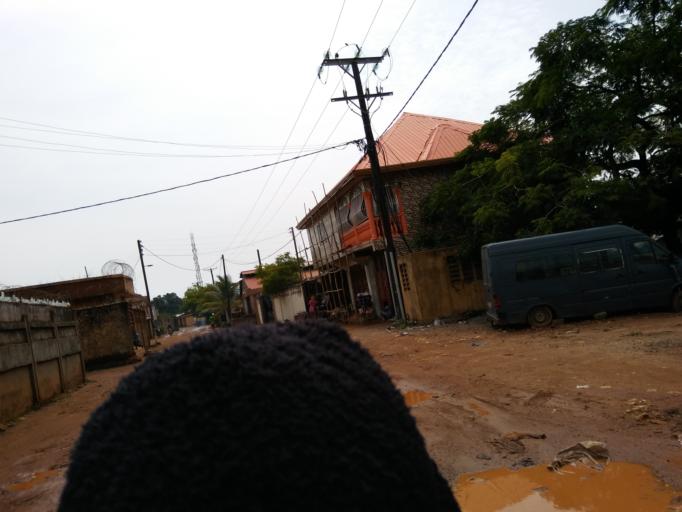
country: SL
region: Western Area
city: Hastings
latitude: 8.3833
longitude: -13.1476
